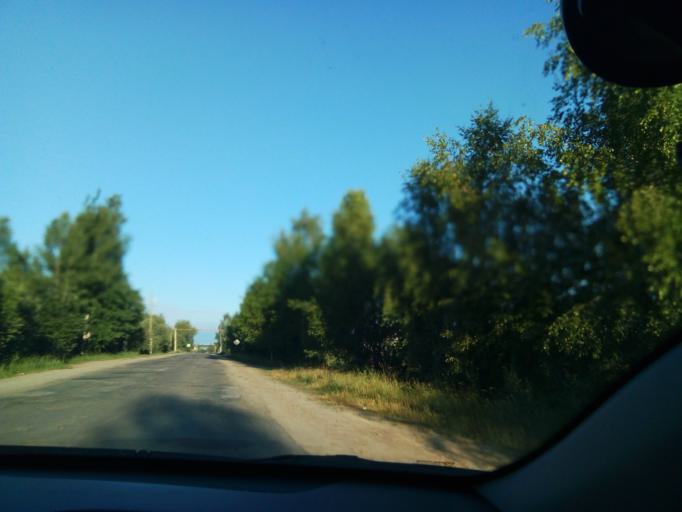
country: RU
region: Nizjnij Novgorod
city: Voznesenskoye
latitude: 54.8894
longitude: 42.7924
